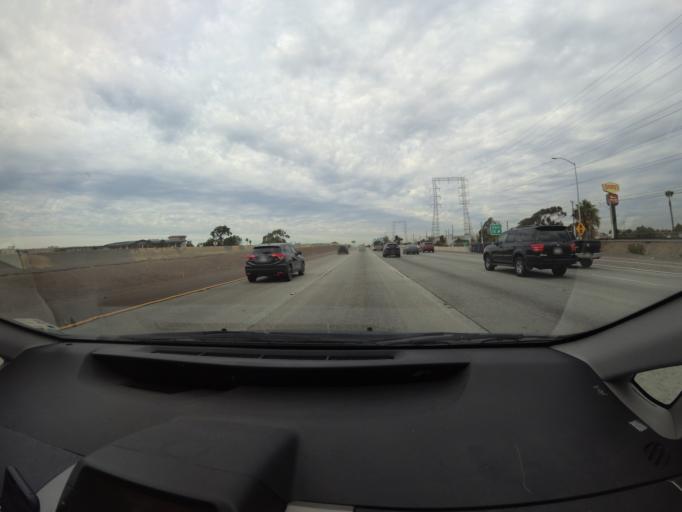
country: US
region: California
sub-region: San Diego County
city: National City
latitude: 32.6585
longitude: -117.1070
